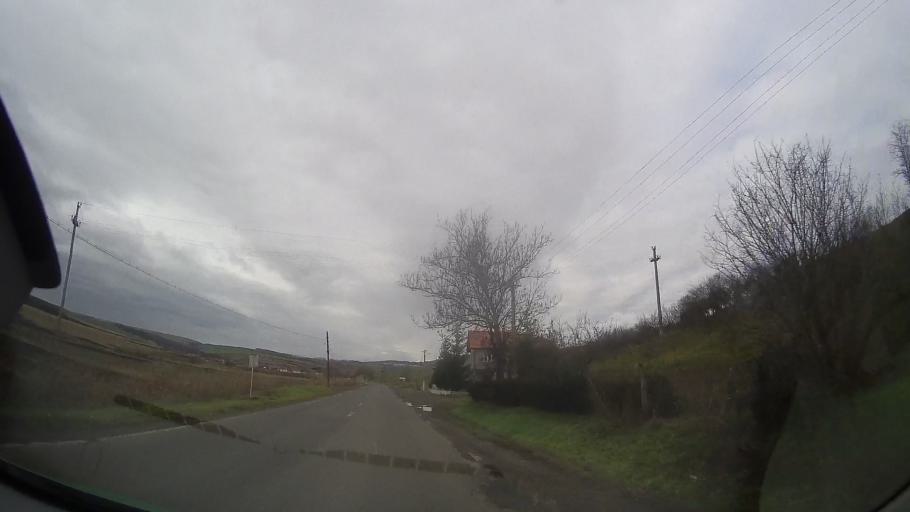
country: RO
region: Bistrita-Nasaud
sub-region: Comuna Urmenis
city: Urmenis
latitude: 46.7676
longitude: 24.3669
